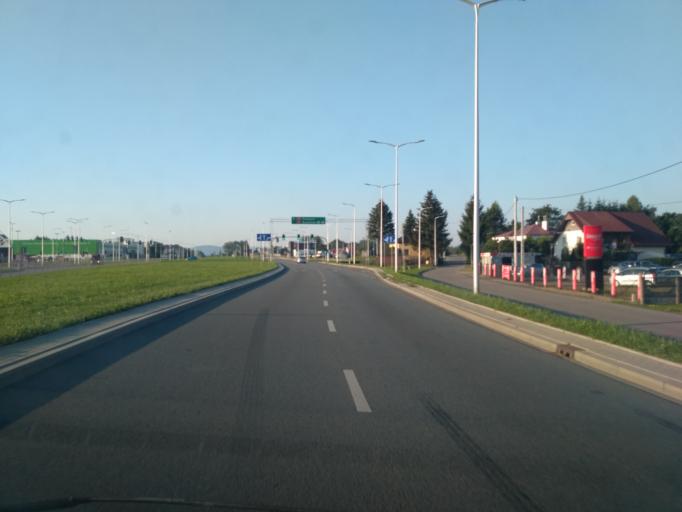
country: PL
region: Subcarpathian Voivodeship
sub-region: Krosno
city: Krosno
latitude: 49.6770
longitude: 21.7738
